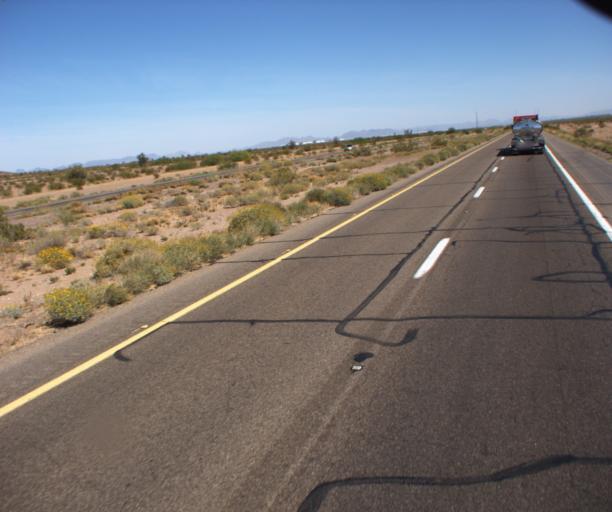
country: US
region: Arizona
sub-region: Maricopa County
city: Gila Bend
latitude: 32.8980
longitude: -113.0192
